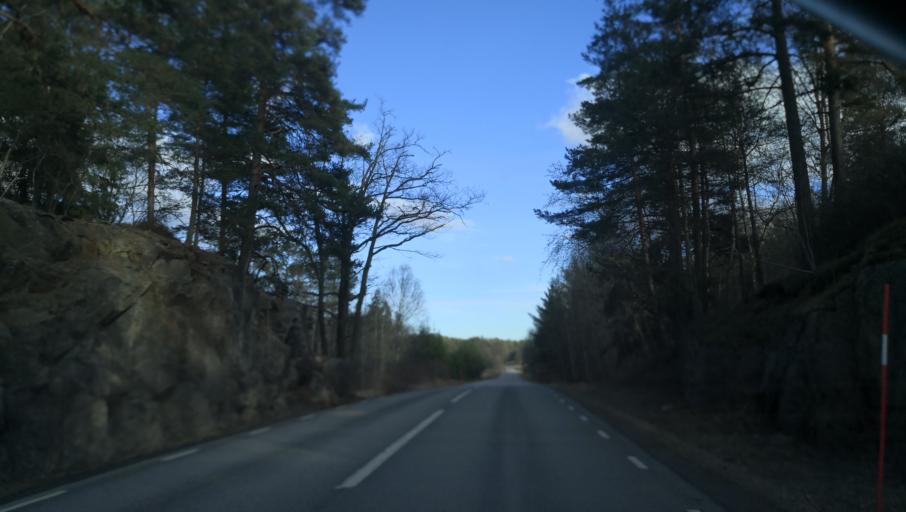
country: SE
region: Stockholm
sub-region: Varmdo Kommun
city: Gustavsberg
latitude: 59.3489
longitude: 18.3725
